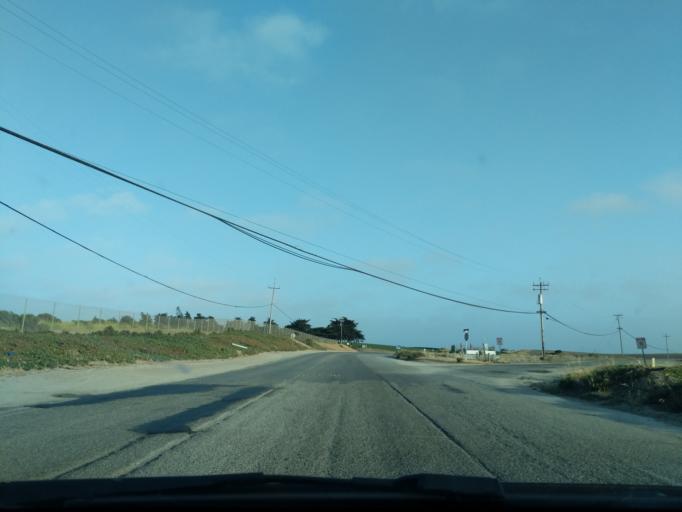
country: US
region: California
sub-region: Monterey County
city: Marina
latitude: 36.7227
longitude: -121.7884
